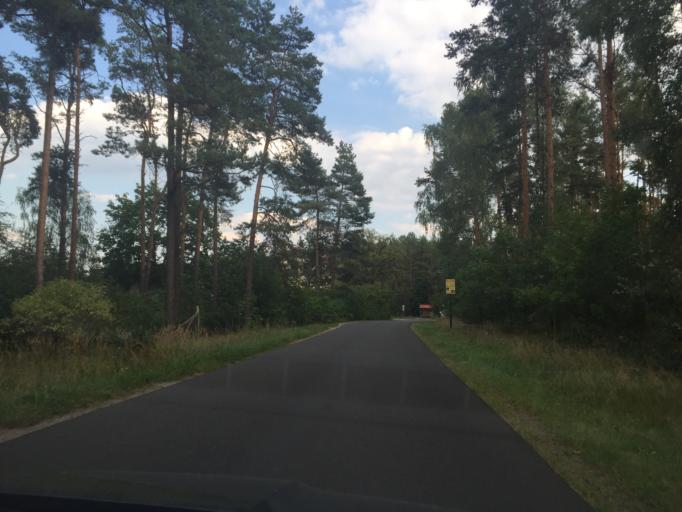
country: DE
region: Brandenburg
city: Erkner
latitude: 52.3737
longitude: 13.7846
